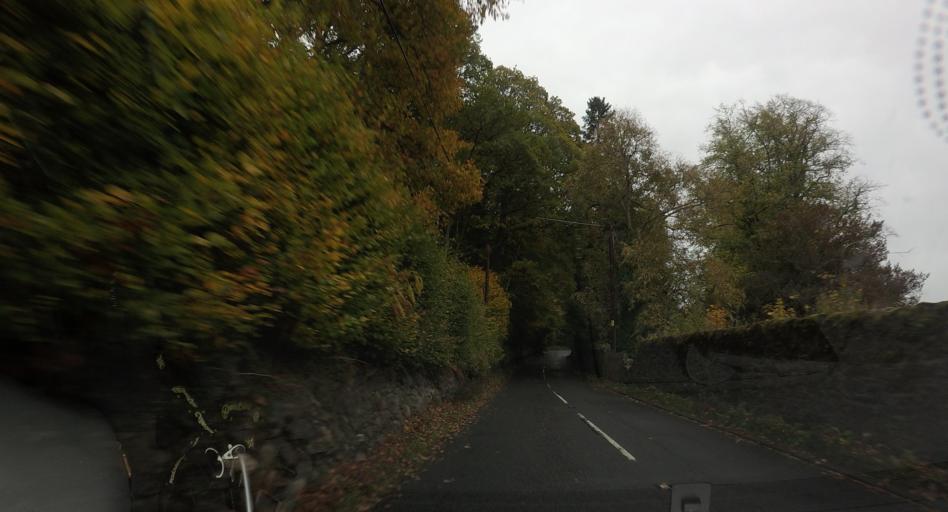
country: GB
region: Scotland
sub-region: Perth and Kinross
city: Bankfoot
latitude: 56.5623
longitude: -3.5749
